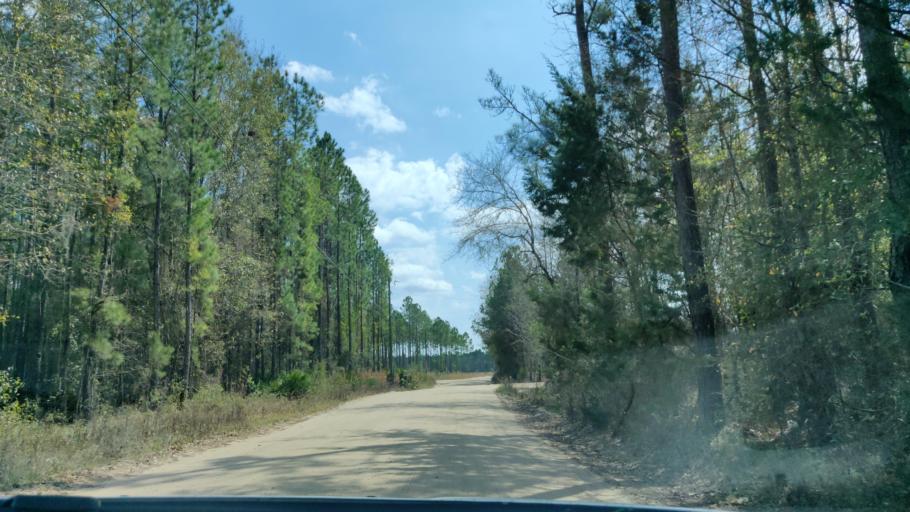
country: US
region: Florida
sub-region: Duval County
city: Baldwin
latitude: 30.1805
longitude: -81.9619
